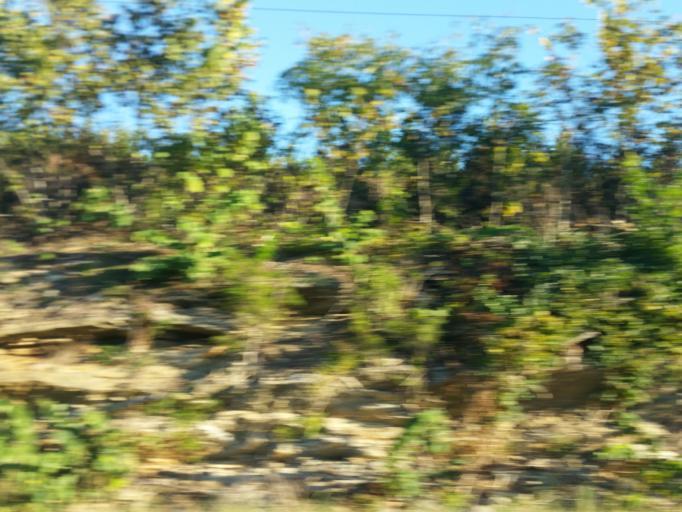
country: US
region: Tennessee
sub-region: Grainger County
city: Bean Station
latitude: 36.3649
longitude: -83.4053
